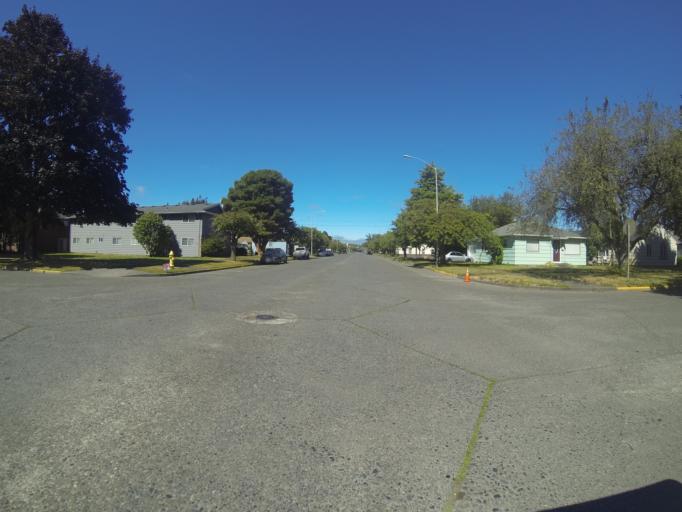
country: US
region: Washington
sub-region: Cowlitz County
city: Longview
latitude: 46.1358
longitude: -122.9281
